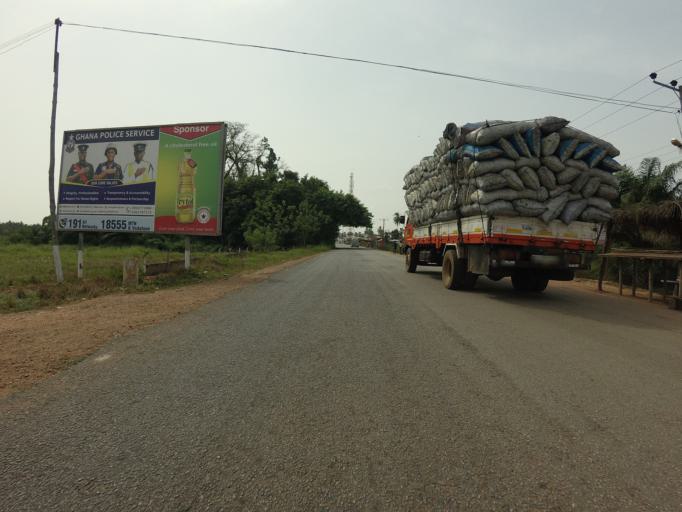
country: GH
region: Volta
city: Ho
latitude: 6.4104
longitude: 0.1725
